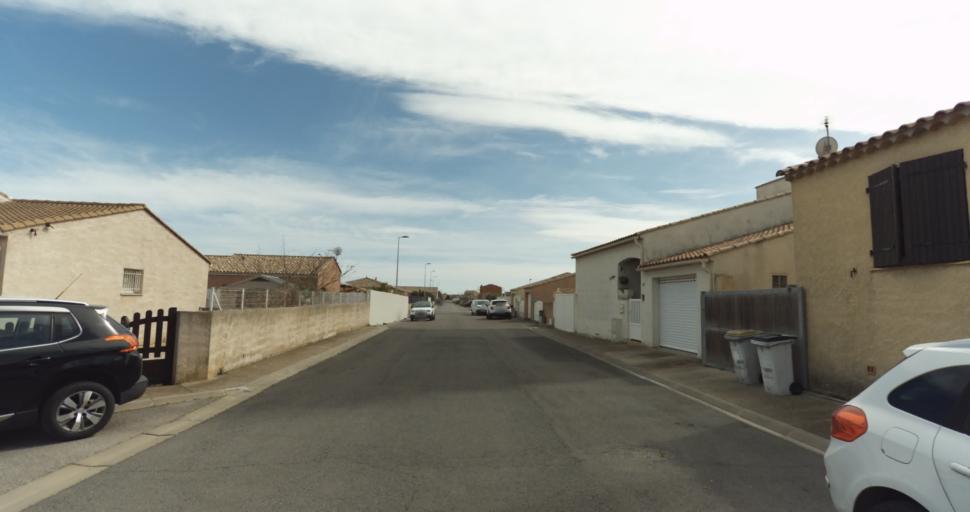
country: FR
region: Languedoc-Roussillon
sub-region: Departement de l'Herault
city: Marseillan
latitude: 43.3422
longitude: 3.5295
